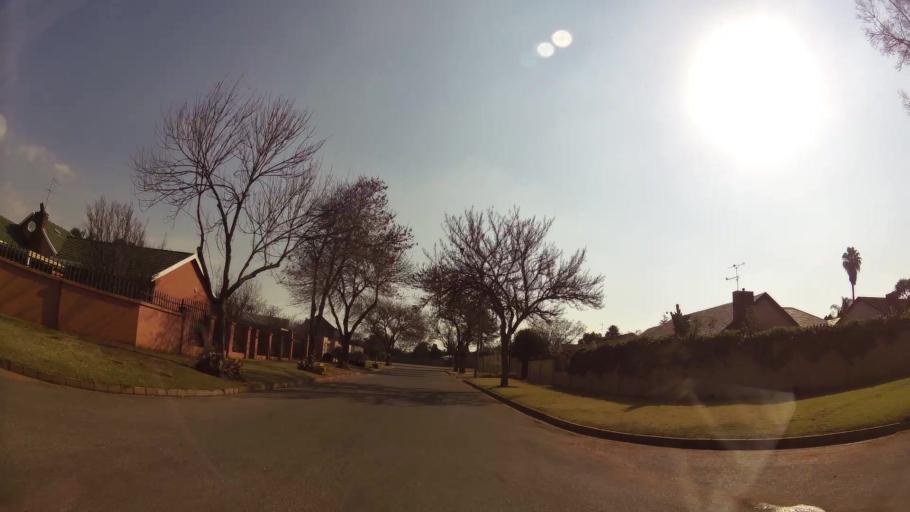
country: ZA
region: Gauteng
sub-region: Ekurhuleni Metropolitan Municipality
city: Boksburg
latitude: -26.1848
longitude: 28.2666
